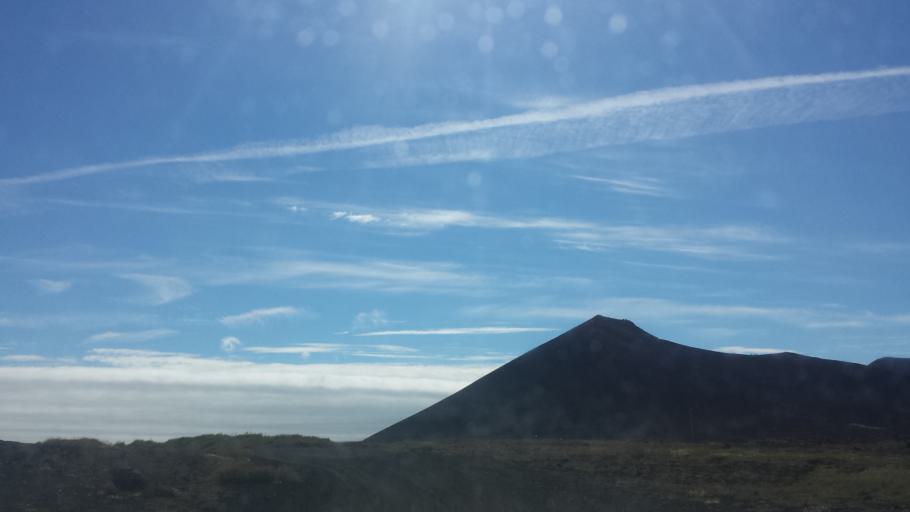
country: IS
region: South
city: Vestmannaeyjar
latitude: 63.4396
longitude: -20.2415
